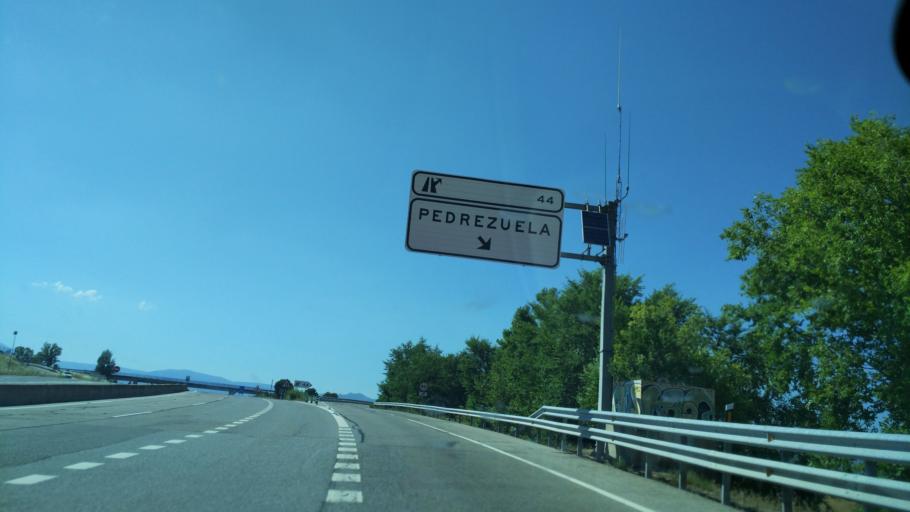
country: ES
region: Madrid
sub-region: Provincia de Madrid
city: El Molar
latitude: 40.7370
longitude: -3.5864
